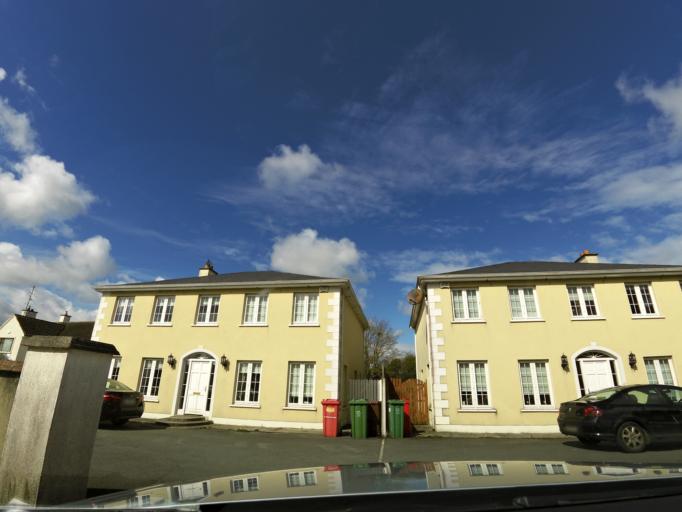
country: IE
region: Munster
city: Thurles
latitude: 52.6780
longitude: -7.7987
